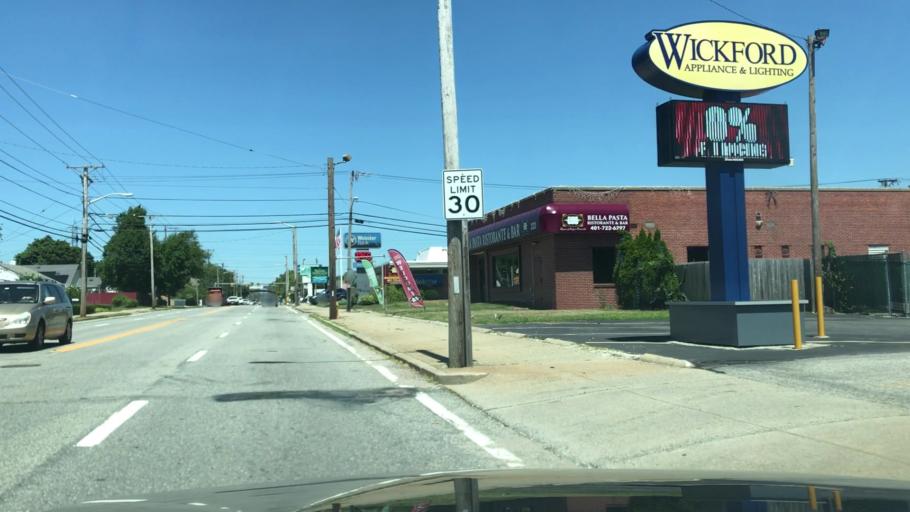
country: US
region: Rhode Island
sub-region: Providence County
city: Pawtucket
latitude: 41.8640
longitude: -71.3544
